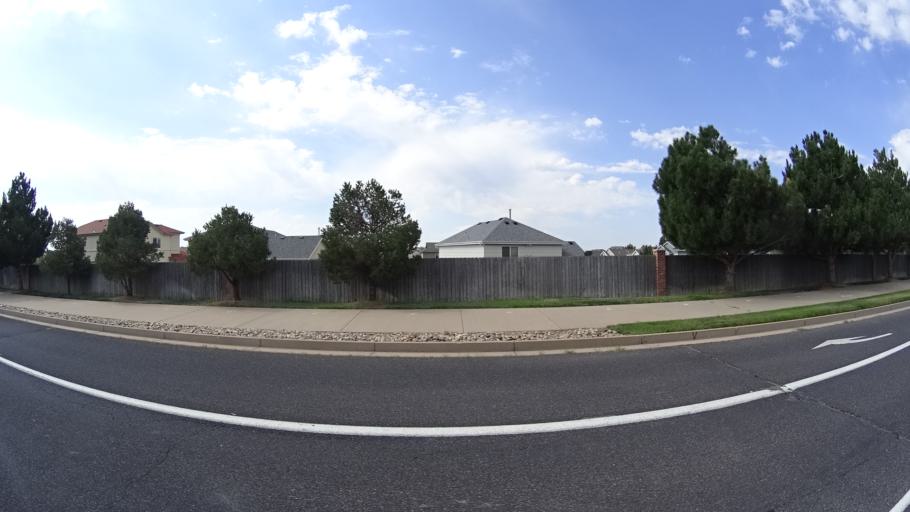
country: US
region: Colorado
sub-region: El Paso County
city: Cimarron Hills
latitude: 38.9123
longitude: -104.6917
